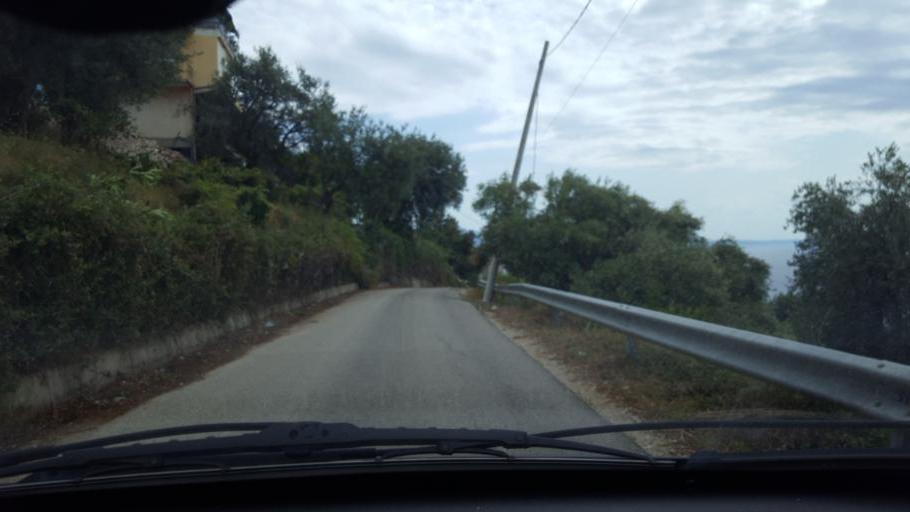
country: AL
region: Vlore
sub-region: Rrethi i Sarandes
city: Lukove
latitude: 39.9889
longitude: 19.9147
